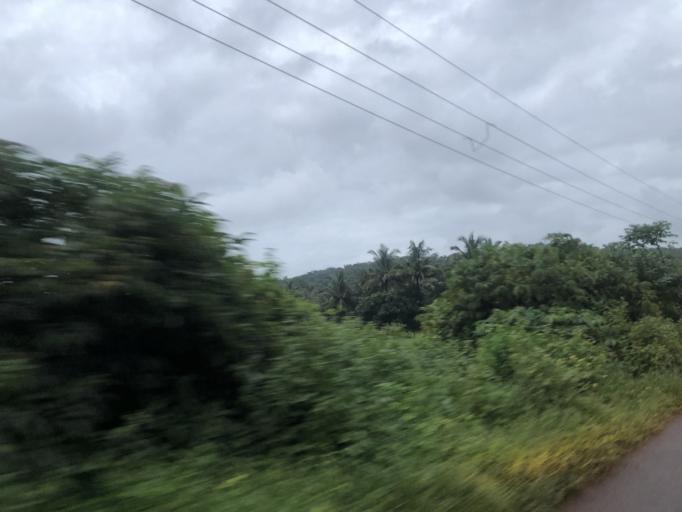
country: IN
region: Goa
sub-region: North Goa
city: Serula
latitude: 15.5522
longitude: 73.8201
